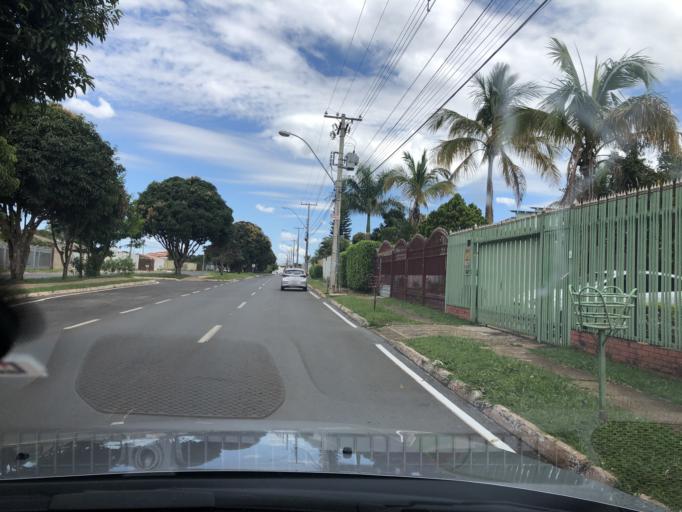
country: BR
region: Federal District
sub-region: Brasilia
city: Brasilia
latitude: -15.9930
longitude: -47.9901
